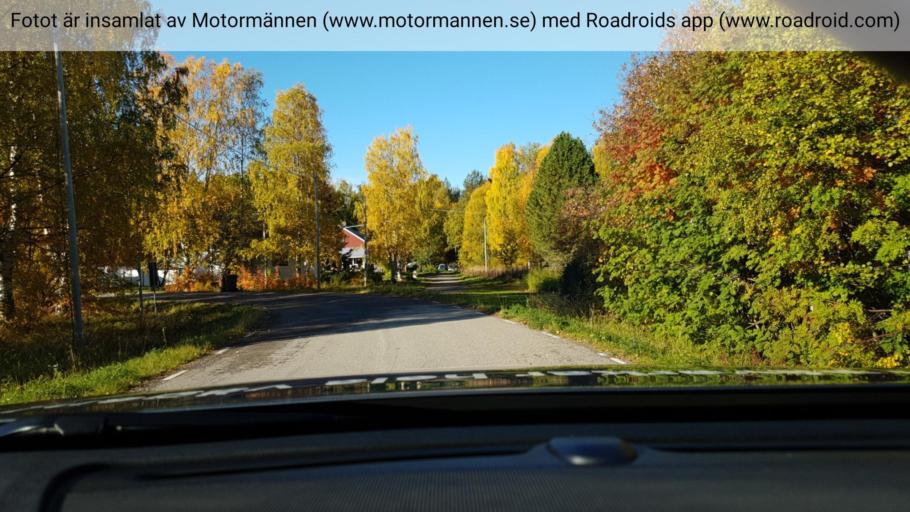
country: SE
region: Norrbotten
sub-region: Alvsbyns Kommun
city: AElvsbyn
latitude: 66.2793
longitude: 21.1236
